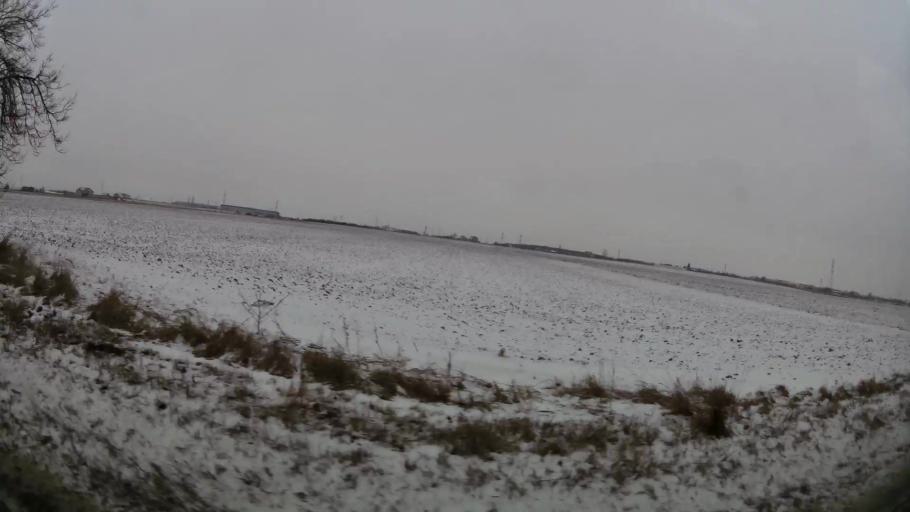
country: RO
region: Dambovita
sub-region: Comuna Ulmi
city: Ulmi
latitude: 44.8901
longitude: 25.5195
